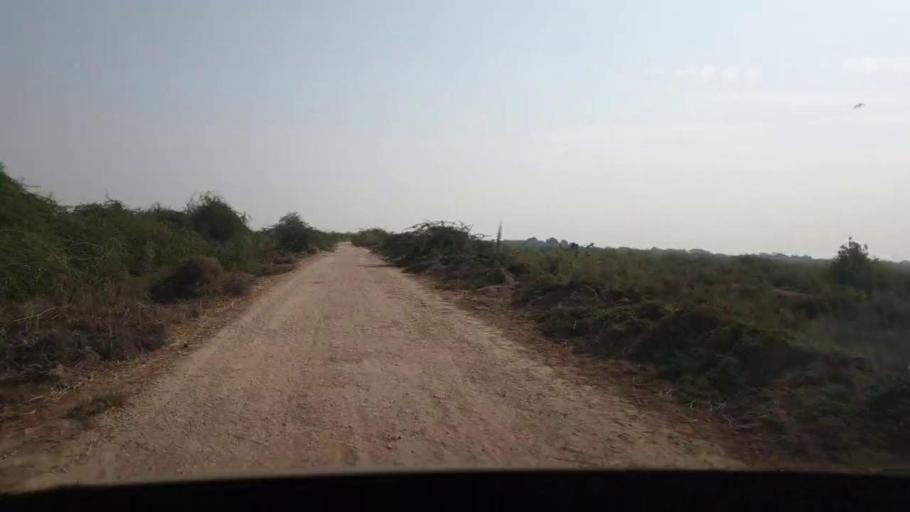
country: PK
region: Sindh
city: Chuhar Jamali
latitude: 24.2489
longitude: 67.9902
